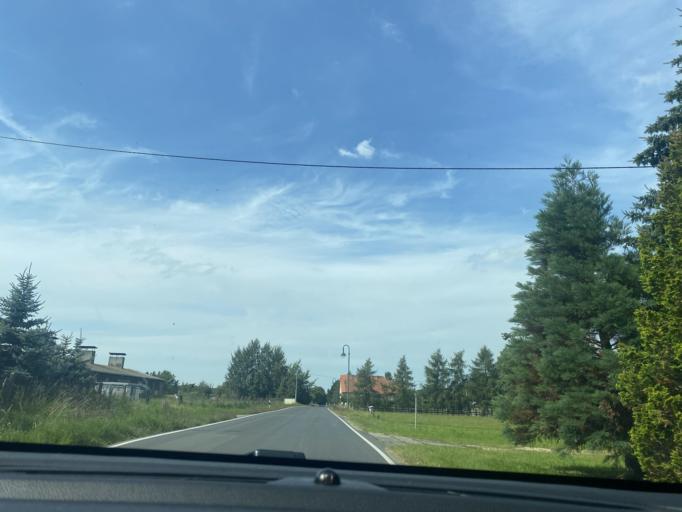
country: DE
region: Saxony
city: Sohland am Rotstein
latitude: 51.0909
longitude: 14.7939
